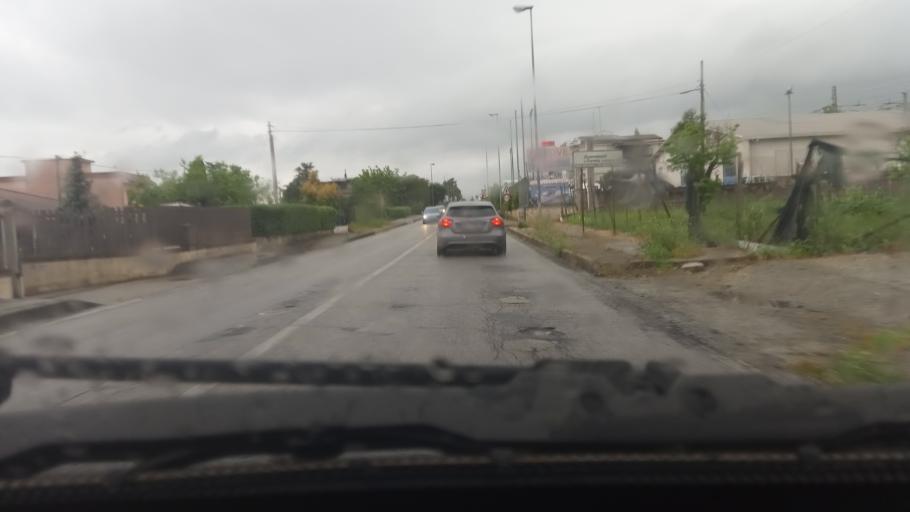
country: IT
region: Latium
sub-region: Provincia di Latina
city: Penitro
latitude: 41.2643
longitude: 13.6761
